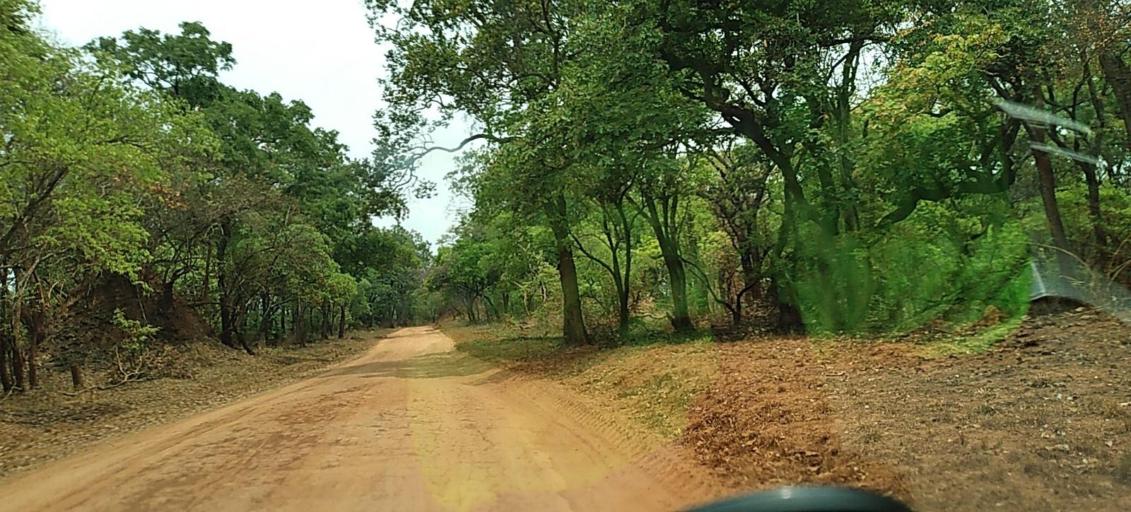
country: ZM
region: North-Western
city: Solwezi
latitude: -12.8085
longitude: 26.5382
